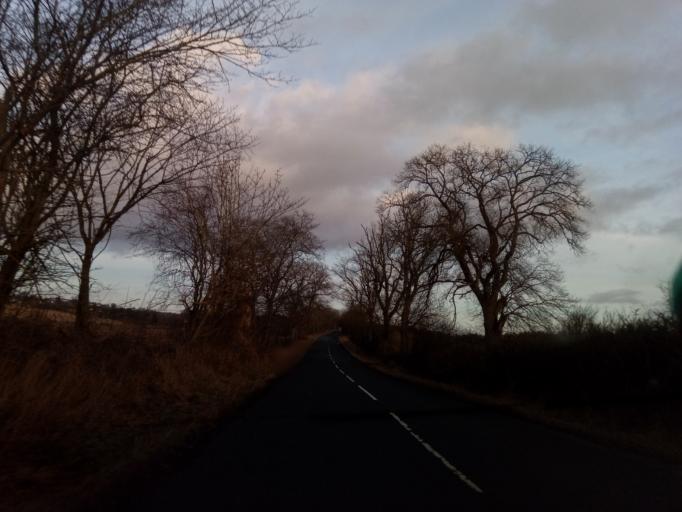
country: GB
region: Scotland
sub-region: The Scottish Borders
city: Melrose
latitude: 55.5573
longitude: -2.7202
